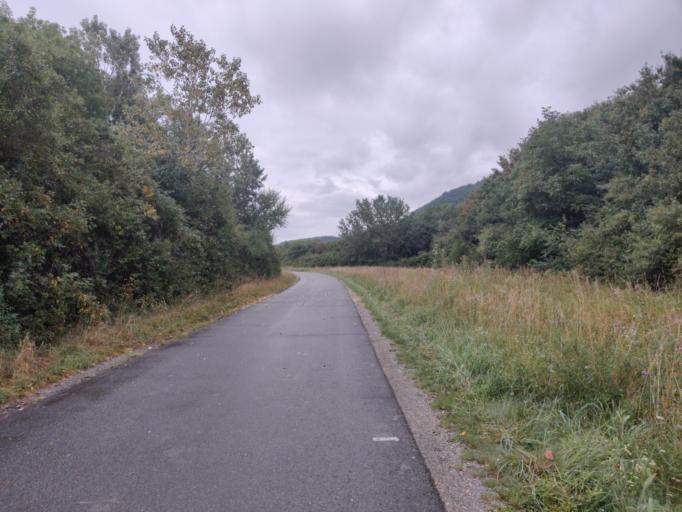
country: AT
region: Lower Austria
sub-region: Politischer Bezirk Korneuburg
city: Langenzersdorf
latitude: 48.2898
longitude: 16.3523
